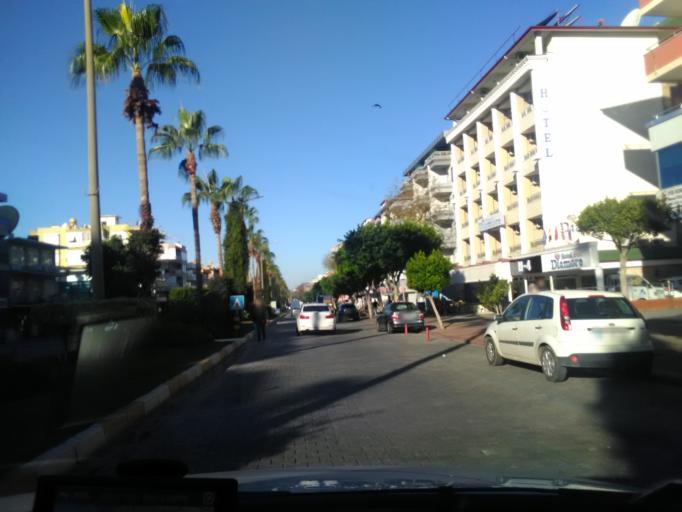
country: TR
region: Antalya
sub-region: Alanya
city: Alanya
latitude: 36.5447
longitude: 31.9948
